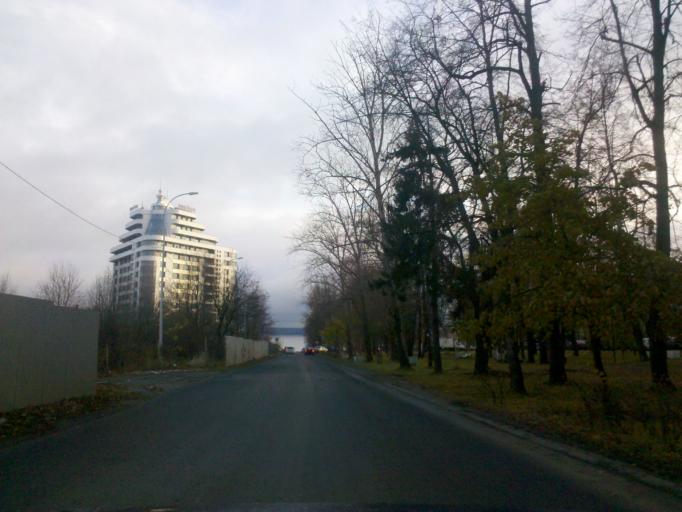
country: RU
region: Republic of Karelia
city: Petrozavodsk
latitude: 61.7940
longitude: 34.3689
